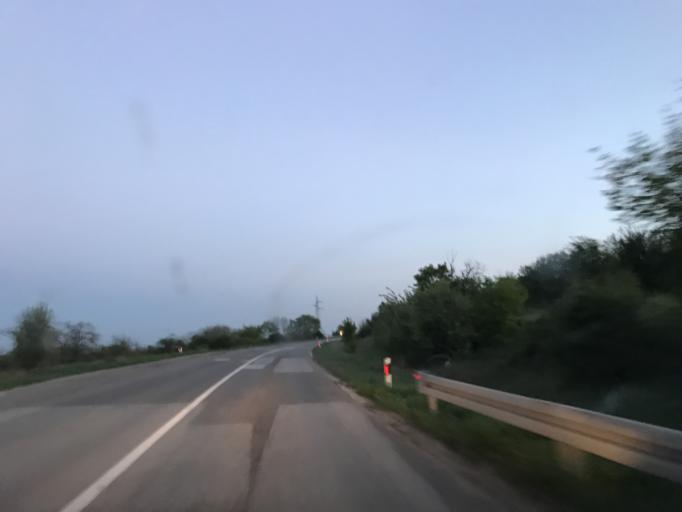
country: RS
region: Central Serbia
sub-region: Zajecarski Okrug
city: Zajecar
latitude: 43.9619
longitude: 22.2990
